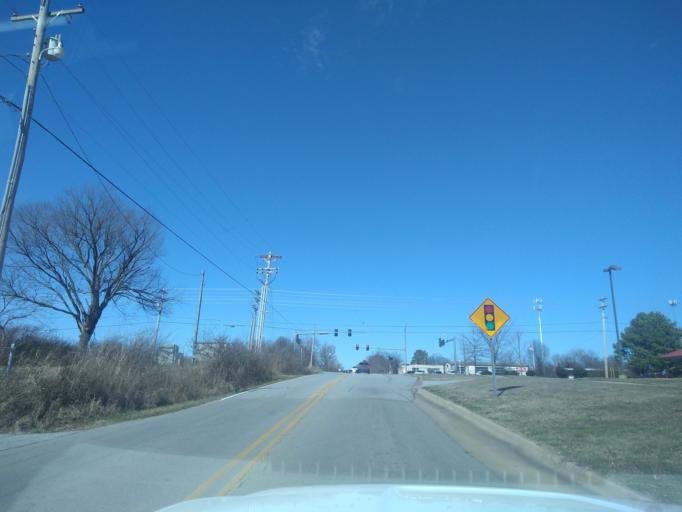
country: US
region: Arkansas
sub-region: Washington County
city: Farmington
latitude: 36.0783
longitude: -94.2531
